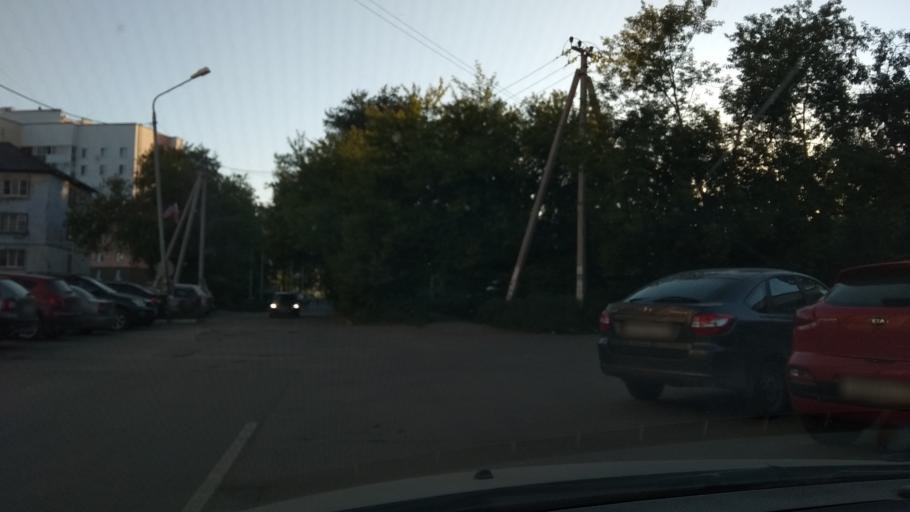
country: RU
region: Sverdlovsk
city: Sredneuralsk
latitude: 56.9889
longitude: 60.4575
